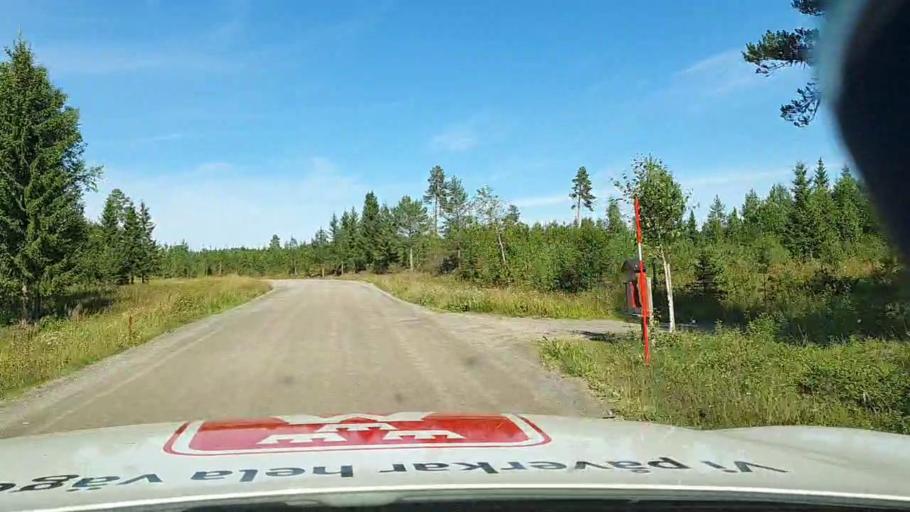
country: SE
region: Jaemtland
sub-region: Stroemsunds Kommun
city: Stroemsund
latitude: 63.6866
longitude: 15.3885
